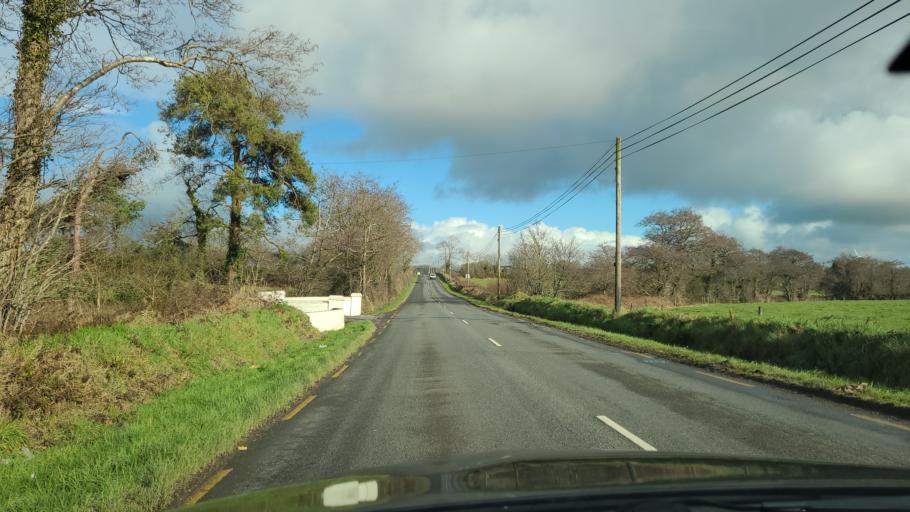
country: IE
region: Munster
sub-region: County Cork
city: Bandon
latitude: 51.7629
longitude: -8.7265
